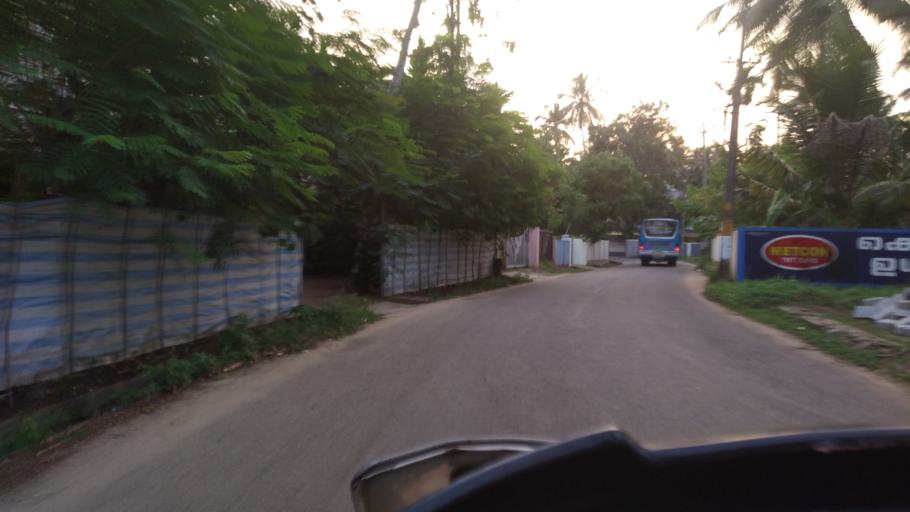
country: IN
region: Kerala
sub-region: Thrissur District
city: Kodungallur
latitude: 10.1801
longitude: 76.2042
